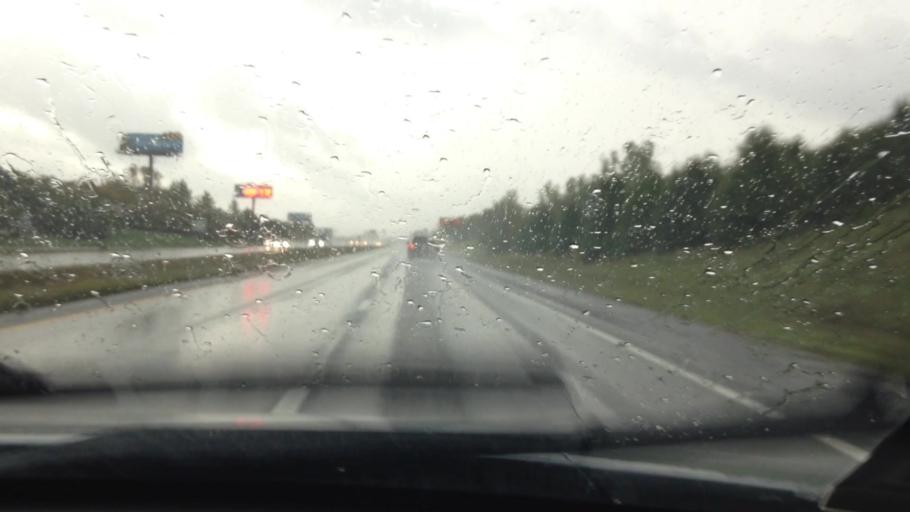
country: US
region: Missouri
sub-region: Platte County
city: Platte City
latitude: 39.3677
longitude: -94.7721
